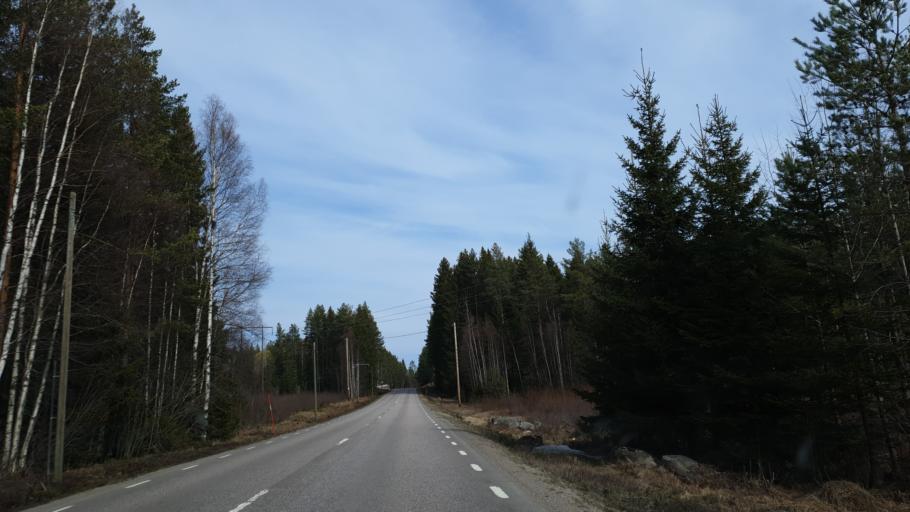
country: SE
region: Gaevleborg
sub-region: Gavle Kommun
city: Norrsundet
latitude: 60.9953
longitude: 17.0871
